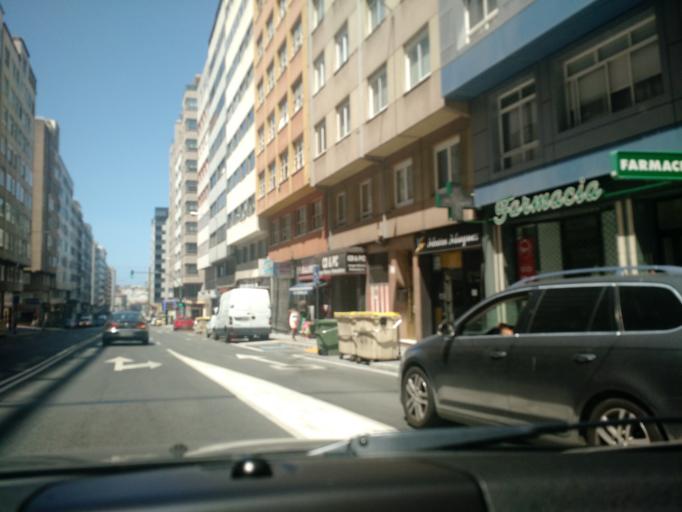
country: ES
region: Galicia
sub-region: Provincia da Coruna
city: A Coruna
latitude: 43.3622
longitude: -8.4162
